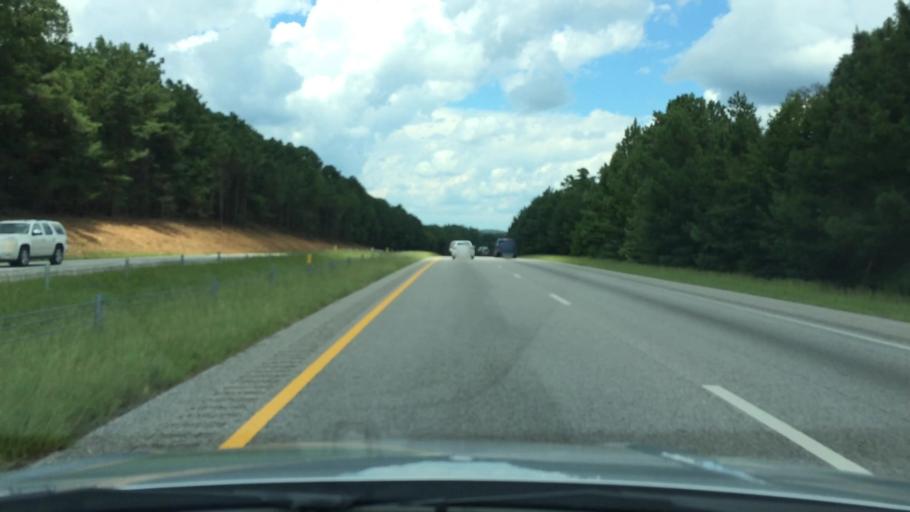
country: US
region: South Carolina
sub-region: Laurens County
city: Clinton
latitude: 34.5753
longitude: -81.8929
